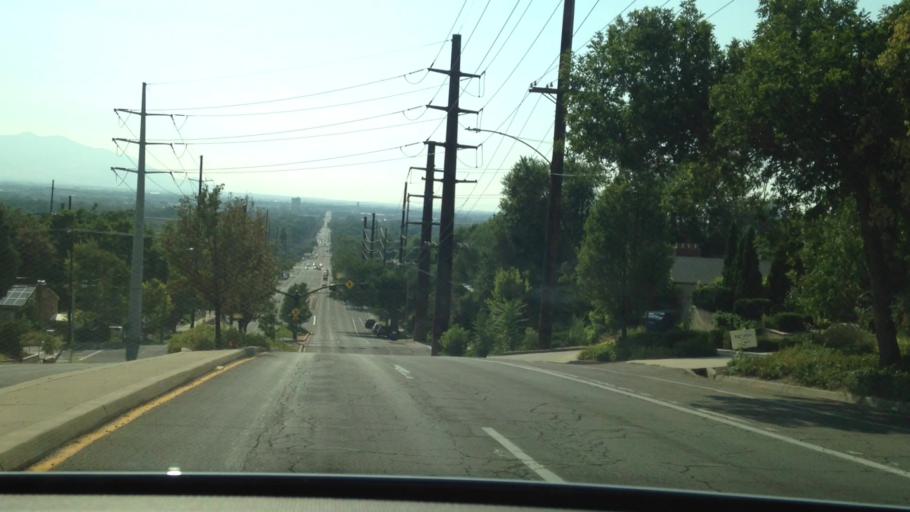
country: US
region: Utah
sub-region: Salt Lake County
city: Salt Lake City
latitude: 40.7520
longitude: -111.8583
